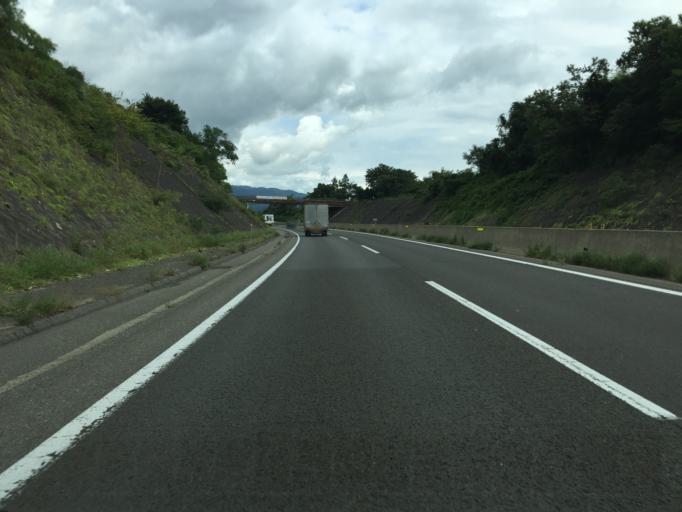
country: JP
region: Fukushima
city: Hobaramachi
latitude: 37.8420
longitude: 140.5035
